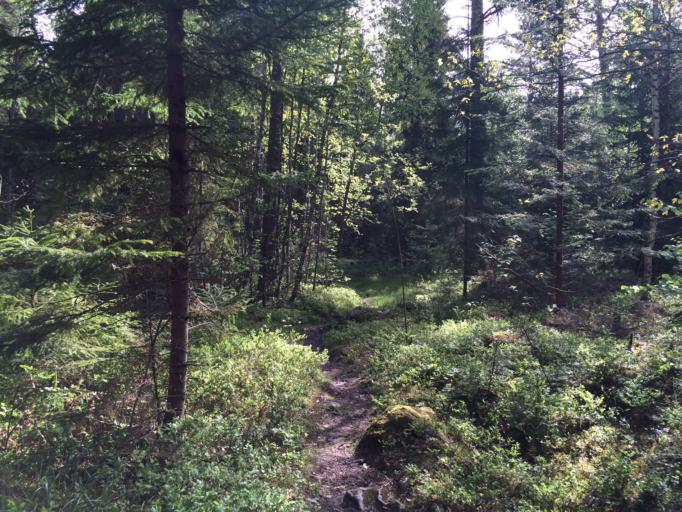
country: SE
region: Vaestmanland
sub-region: Hallstahammars Kommun
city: Hallstahammar
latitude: 59.6169
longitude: 16.2615
